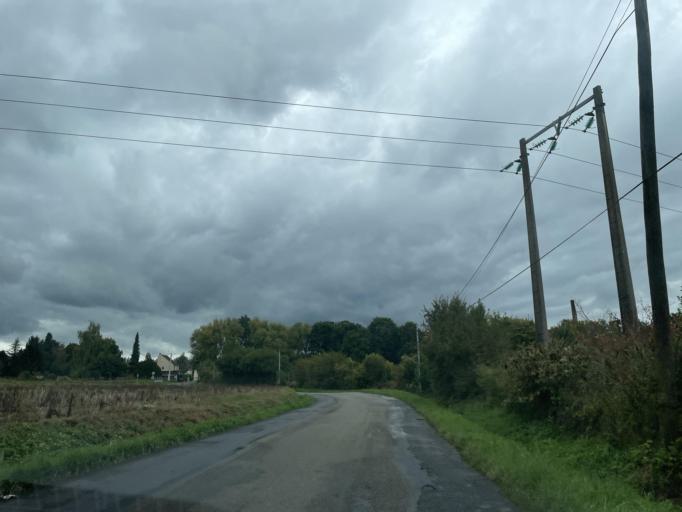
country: FR
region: Ile-de-France
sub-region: Departement de Seine-et-Marne
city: Chailly-en-Brie
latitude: 48.8091
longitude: 3.1158
